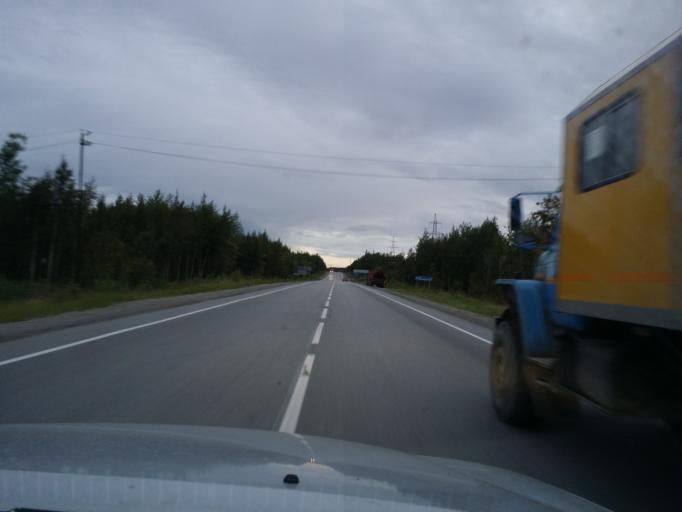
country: RU
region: Khanty-Mansiyskiy Avtonomnyy Okrug
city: Nizhnevartovsk
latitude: 60.9709
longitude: 76.7037
